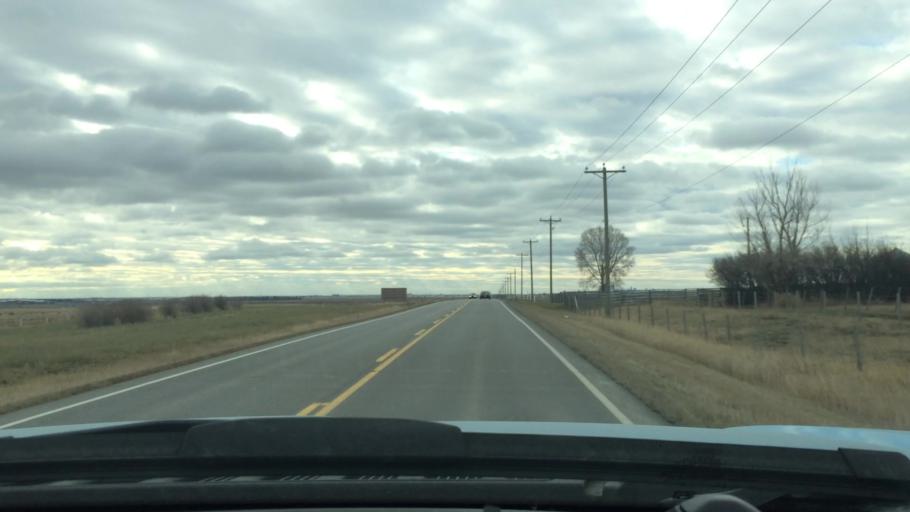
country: CA
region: Alberta
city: Airdrie
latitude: 51.2288
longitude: -114.0250
